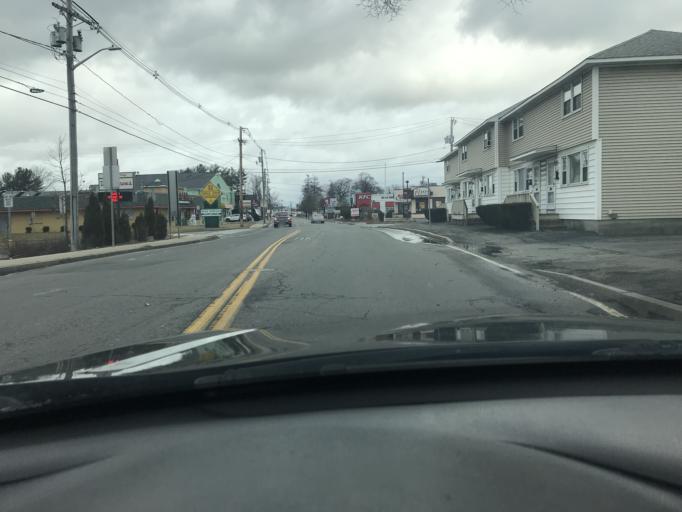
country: US
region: Massachusetts
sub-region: Middlesex County
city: Chelmsford
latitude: 42.6348
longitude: -71.3547
